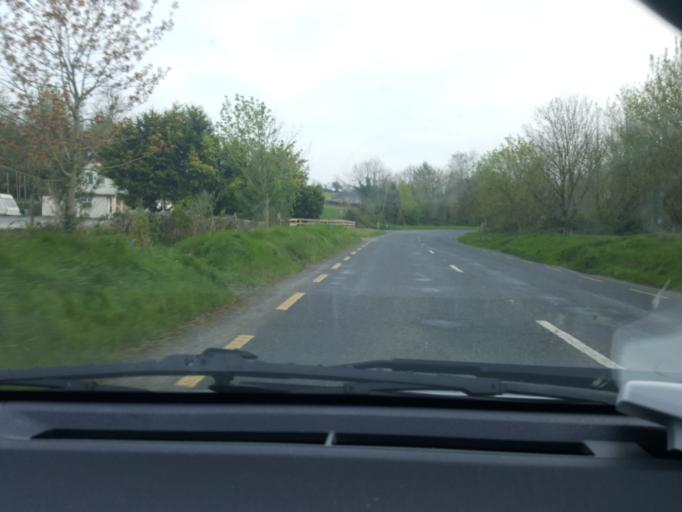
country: IE
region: Munster
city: Cahir
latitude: 52.3888
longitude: -7.9116
